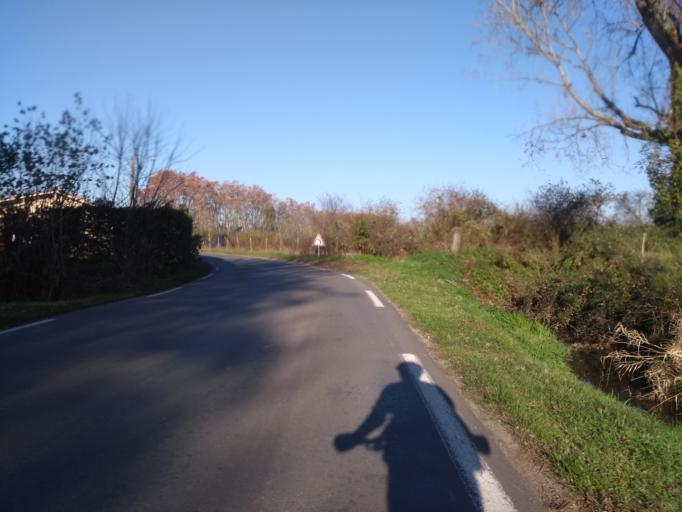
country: FR
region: Aquitaine
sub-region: Departement de la Gironde
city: Martillac
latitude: 44.7268
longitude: -0.5120
